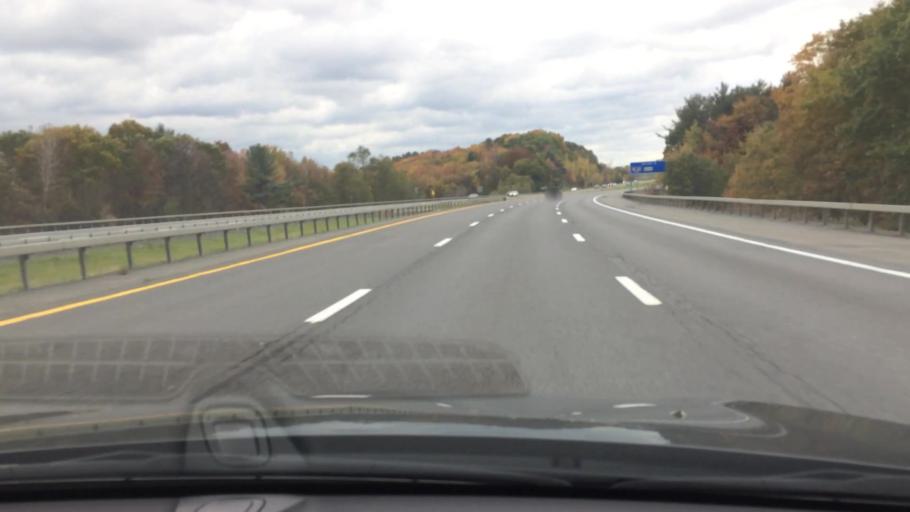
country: US
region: New York
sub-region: Rensselaer County
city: East Greenbush
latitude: 42.5883
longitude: -73.6770
